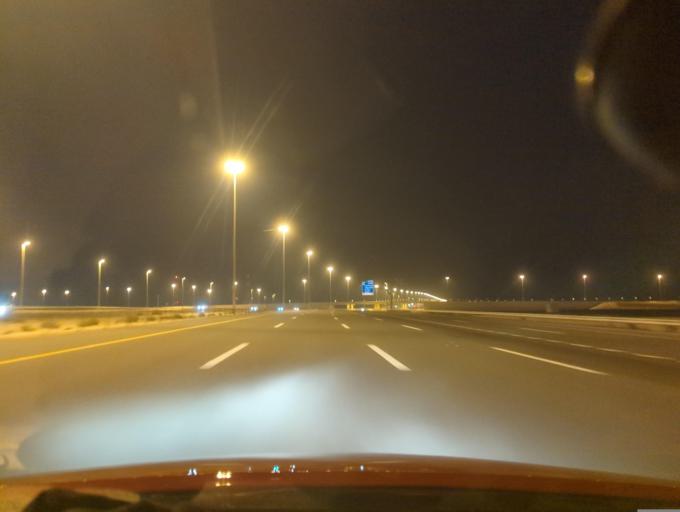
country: AE
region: Abu Dhabi
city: Abu Dhabi
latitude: 24.4544
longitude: 54.7503
